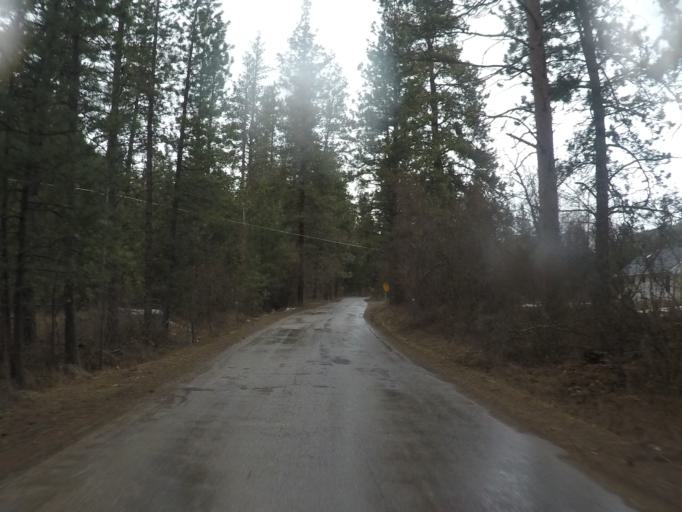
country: US
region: Montana
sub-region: Missoula County
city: East Missoula
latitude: 46.9190
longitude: -113.9597
